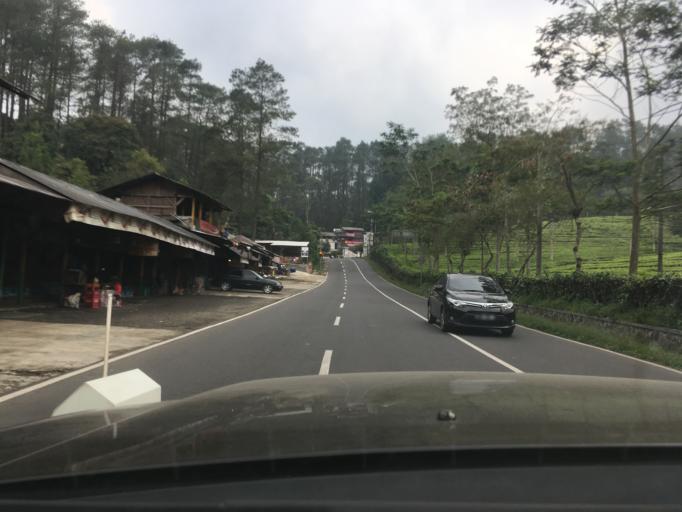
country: ID
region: West Java
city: Lembang
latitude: -6.7725
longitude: 107.6370
